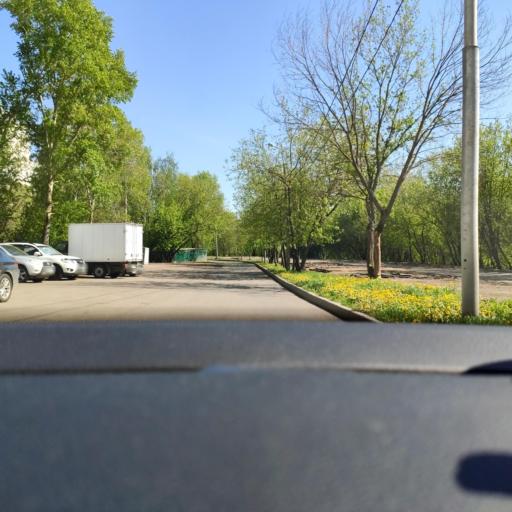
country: RU
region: Moscow
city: Kozeyevo
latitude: 55.8724
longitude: 37.6231
